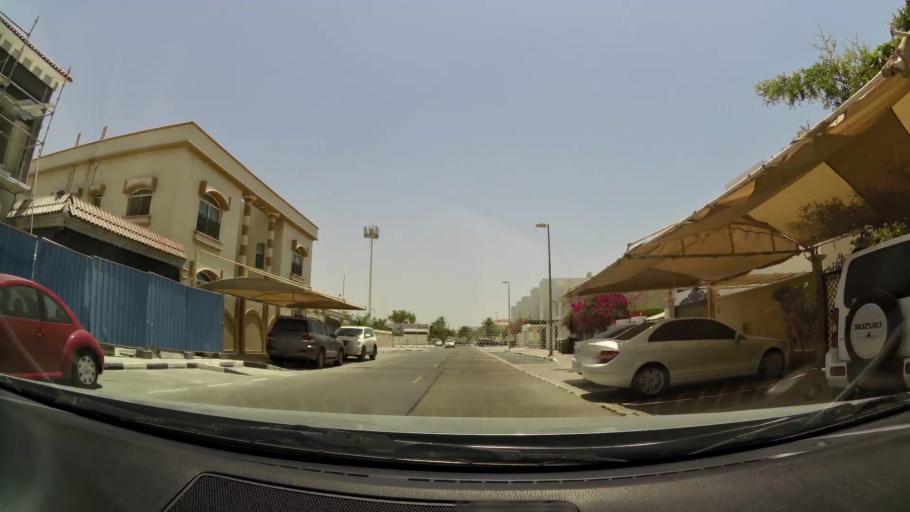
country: AE
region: Dubai
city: Dubai
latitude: 25.2216
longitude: 55.2574
